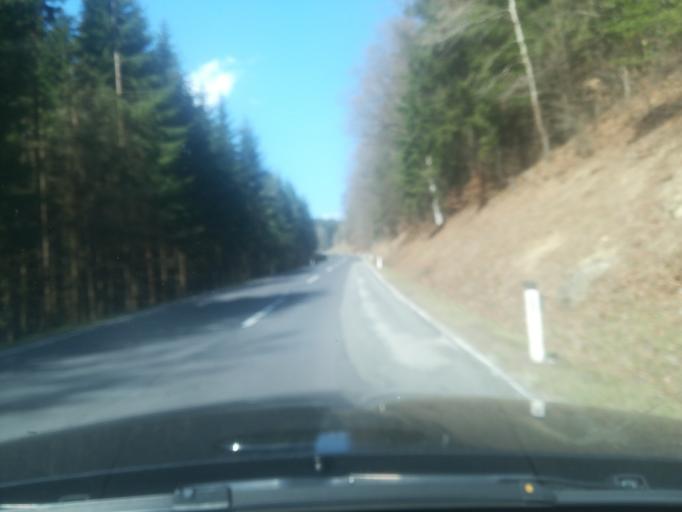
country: AT
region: Upper Austria
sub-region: Politischer Bezirk Perg
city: Bad Kreuzen
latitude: 48.4033
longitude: 14.7318
